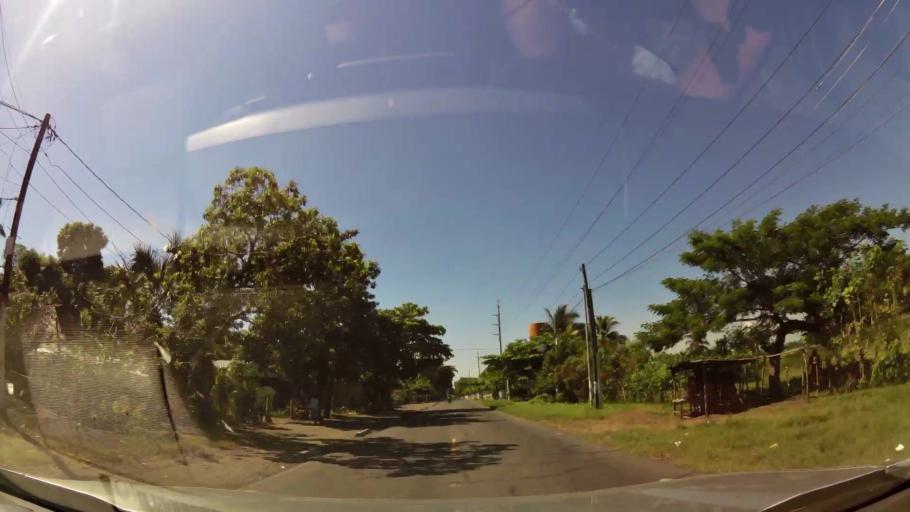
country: GT
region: Escuintla
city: Iztapa
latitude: 13.9373
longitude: -90.7278
